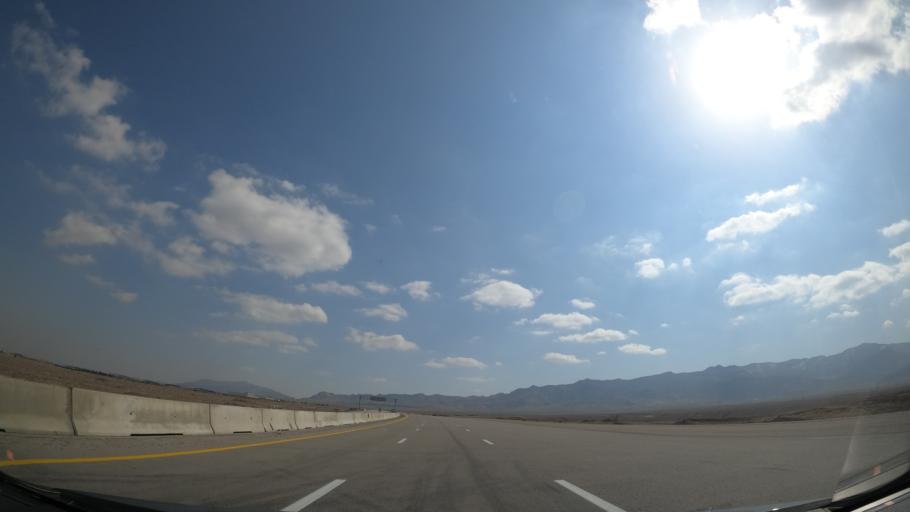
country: IR
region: Alborz
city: Eshtehard
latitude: 35.7265
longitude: 50.5634
